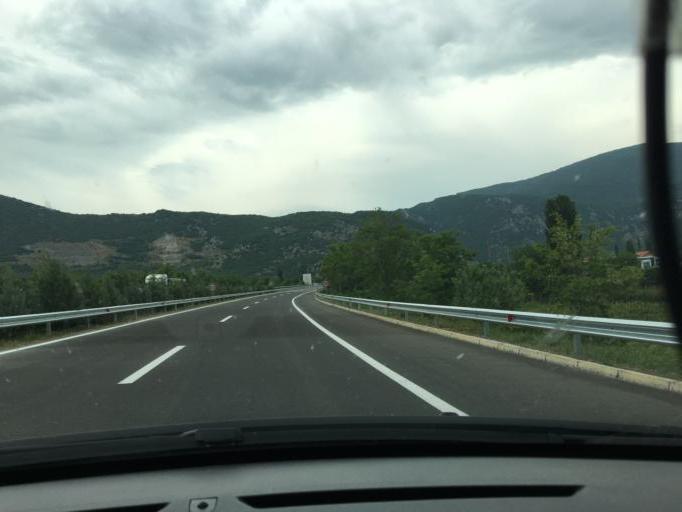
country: MK
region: Demir Kapija
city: Demir Kapija
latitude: 41.4154
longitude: 22.2397
